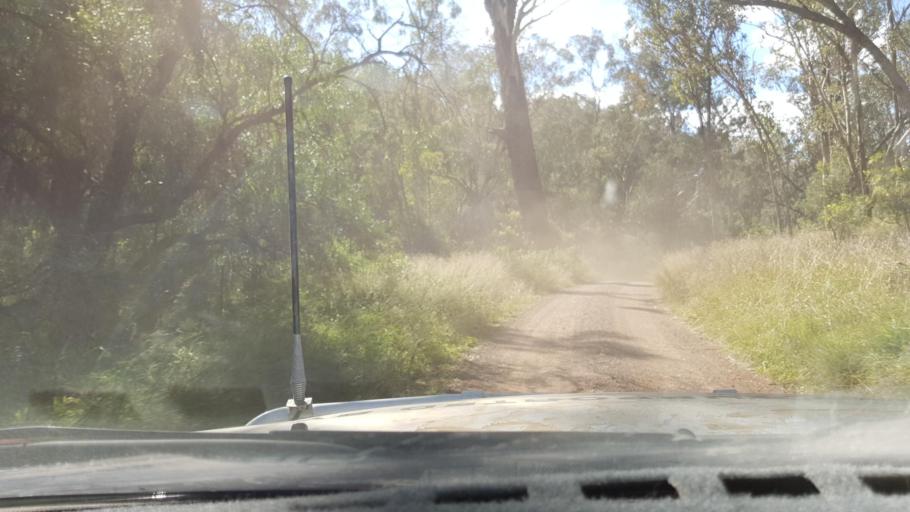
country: AU
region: New South Wales
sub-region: Tamworth Municipality
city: Manilla
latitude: -30.4807
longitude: 150.7683
